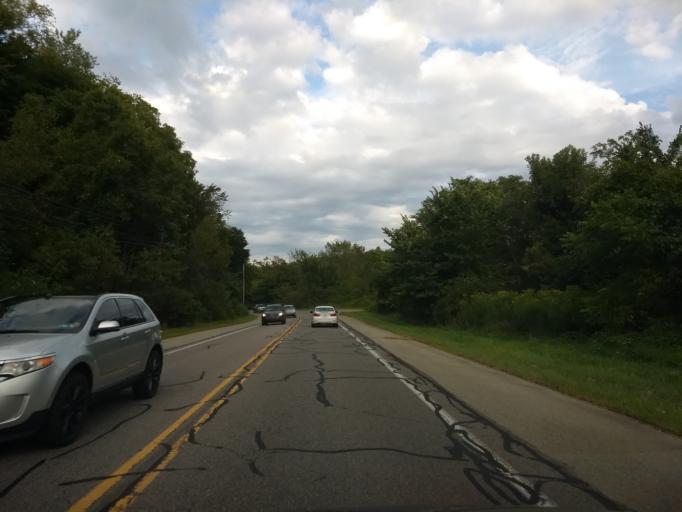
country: US
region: Pennsylvania
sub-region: Allegheny County
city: Coraopolis
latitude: 40.4622
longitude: -80.1655
